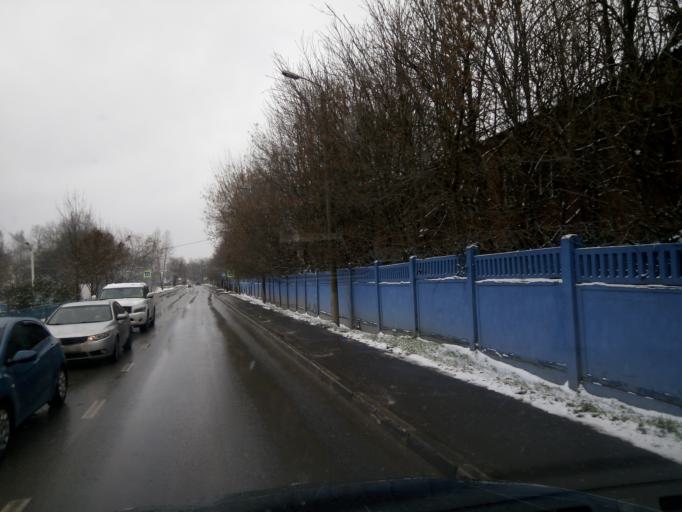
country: RU
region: Moskovskaya
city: Skhodnya
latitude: 55.9426
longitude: 37.2794
